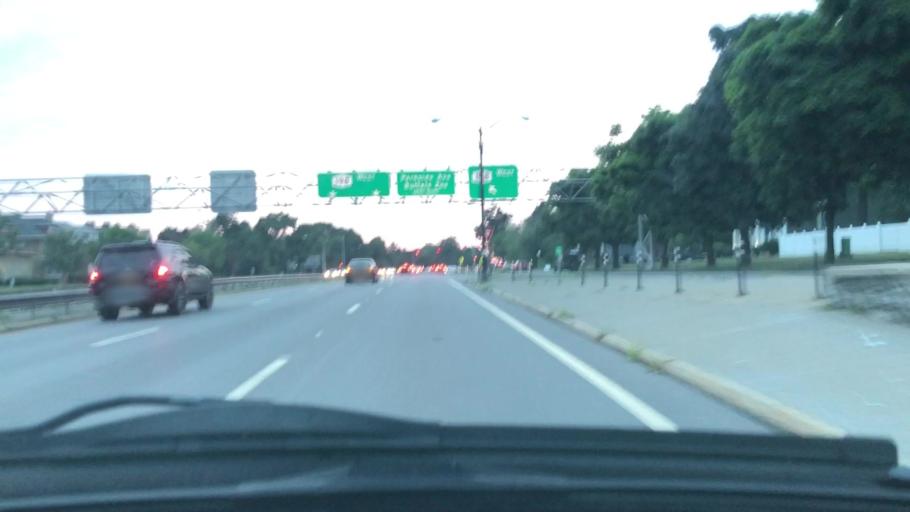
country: US
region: New York
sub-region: Erie County
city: Kenmore
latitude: 42.9290
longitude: -78.8525
